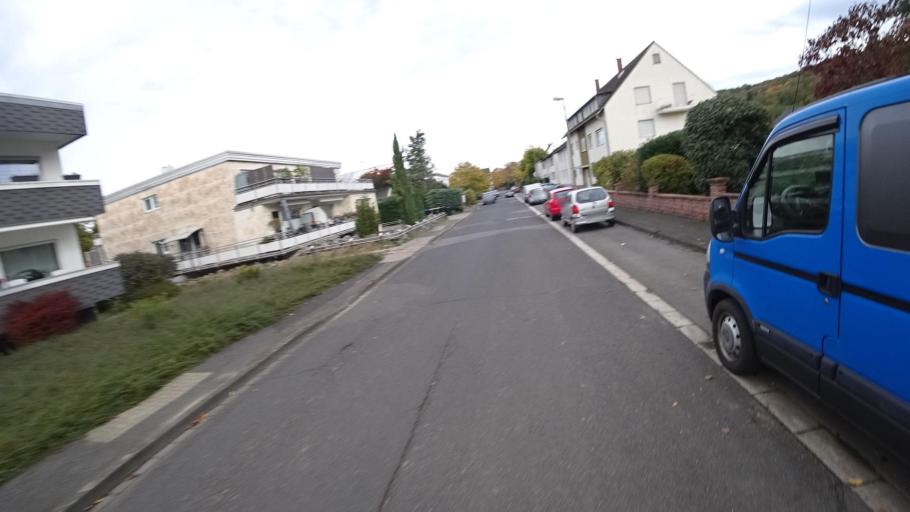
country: DE
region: Rheinland-Pfalz
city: Remagen
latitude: 50.5492
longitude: 7.2112
